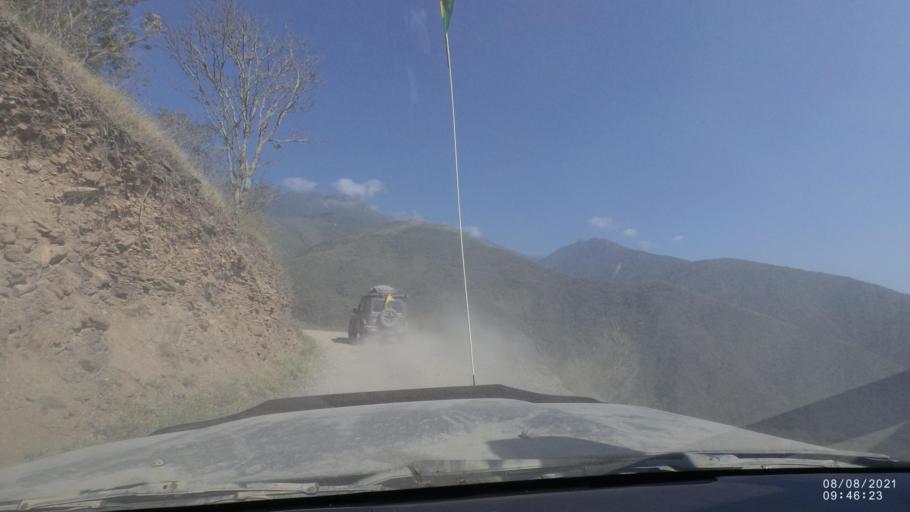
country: BO
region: La Paz
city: Quime
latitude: -16.6052
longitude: -66.7302
